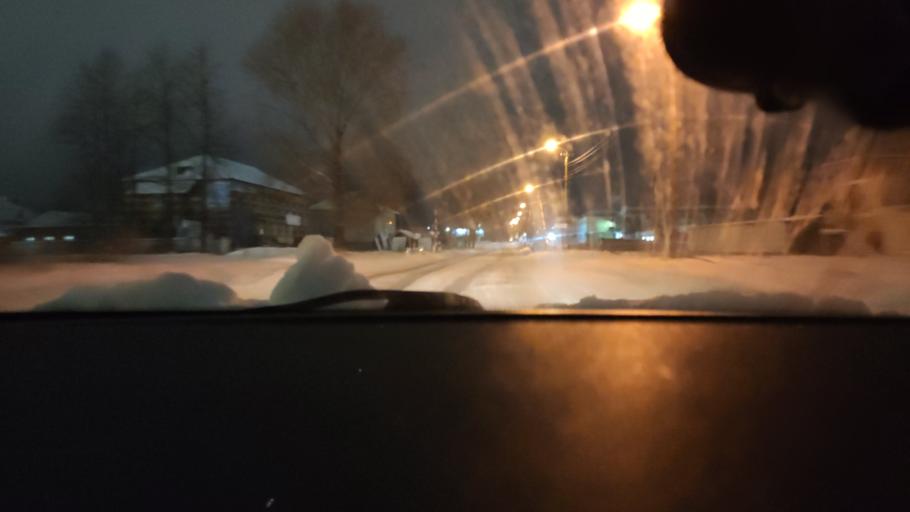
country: RU
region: Perm
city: Krasnokamsk
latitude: 58.0802
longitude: 55.7723
